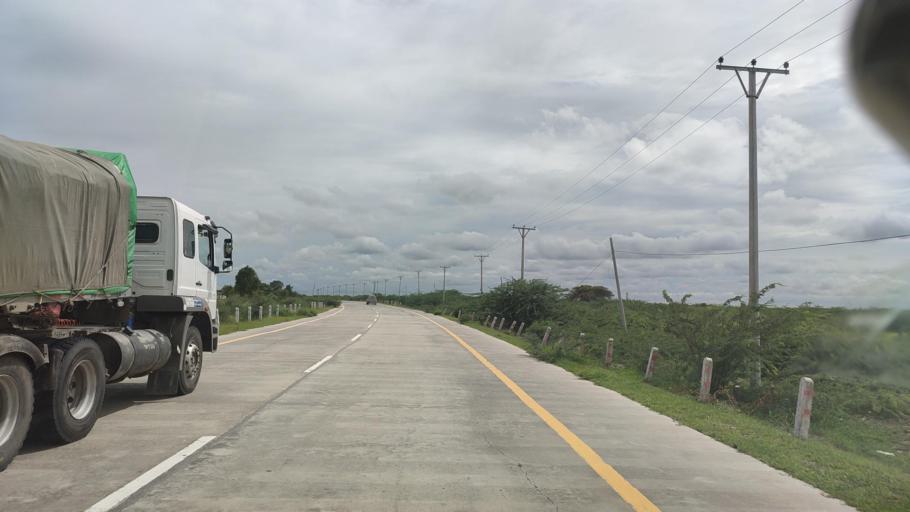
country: MM
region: Mandalay
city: Meiktila
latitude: 21.0377
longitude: 95.9942
